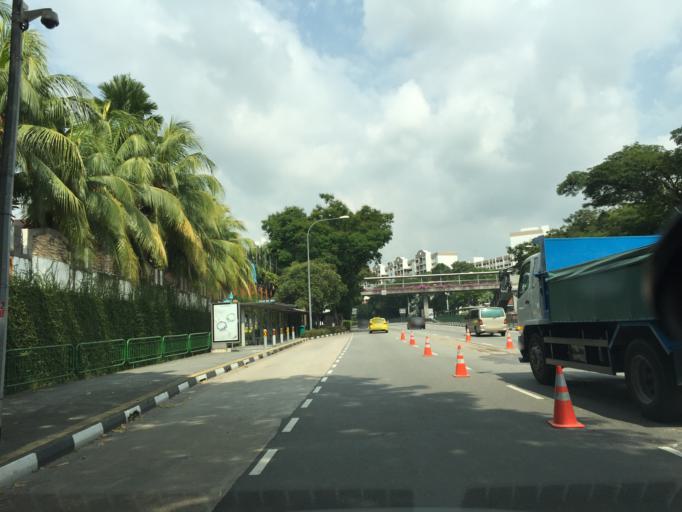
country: SG
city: Singapore
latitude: 1.3197
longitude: 103.8110
